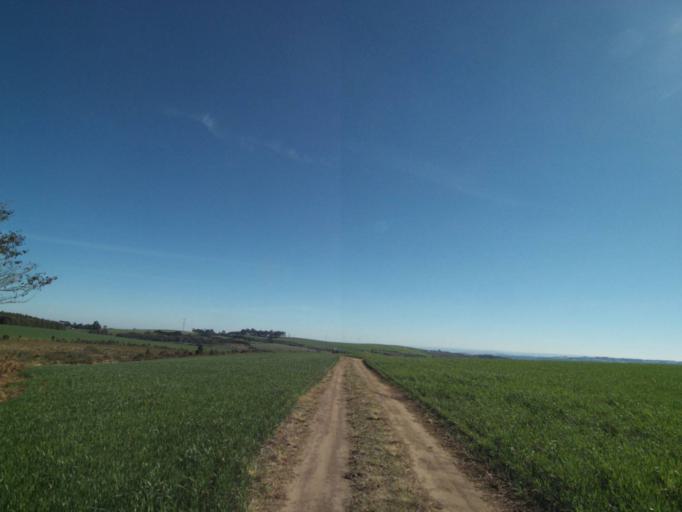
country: BR
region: Parana
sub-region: Tibagi
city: Tibagi
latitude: -24.5918
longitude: -50.2499
